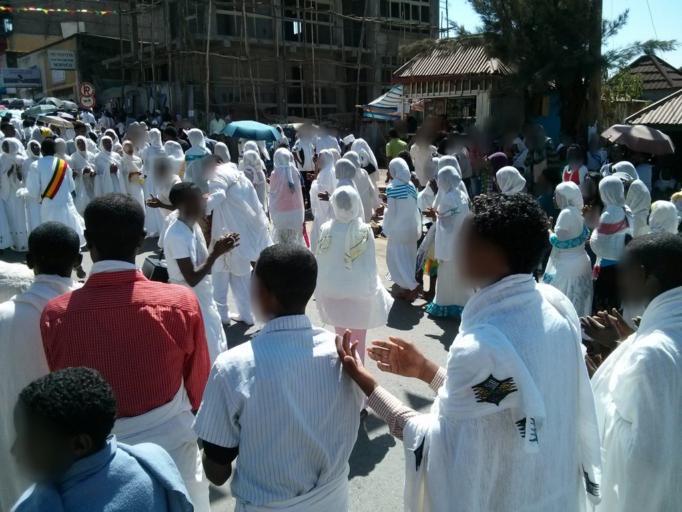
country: ET
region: Amhara
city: Gondar
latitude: 12.6132
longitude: 37.4674
